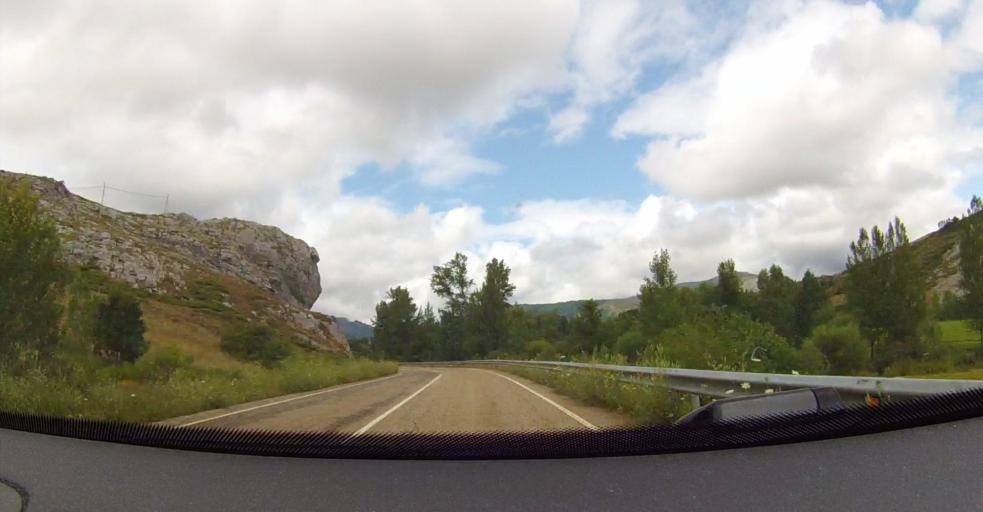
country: ES
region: Castille and Leon
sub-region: Provincia de Leon
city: Puebla de Lillo
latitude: 42.9928
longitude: -5.2623
